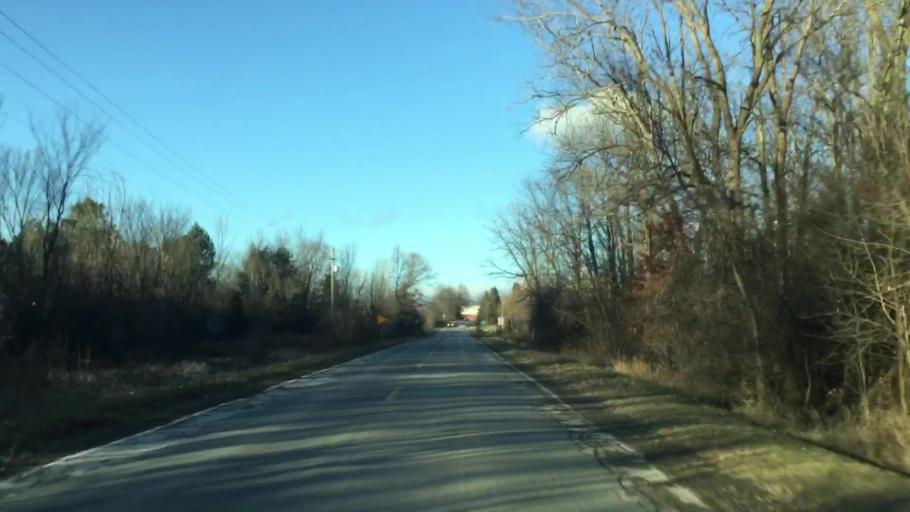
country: US
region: Michigan
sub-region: Genesee County
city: Linden
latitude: 42.7800
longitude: -83.7864
